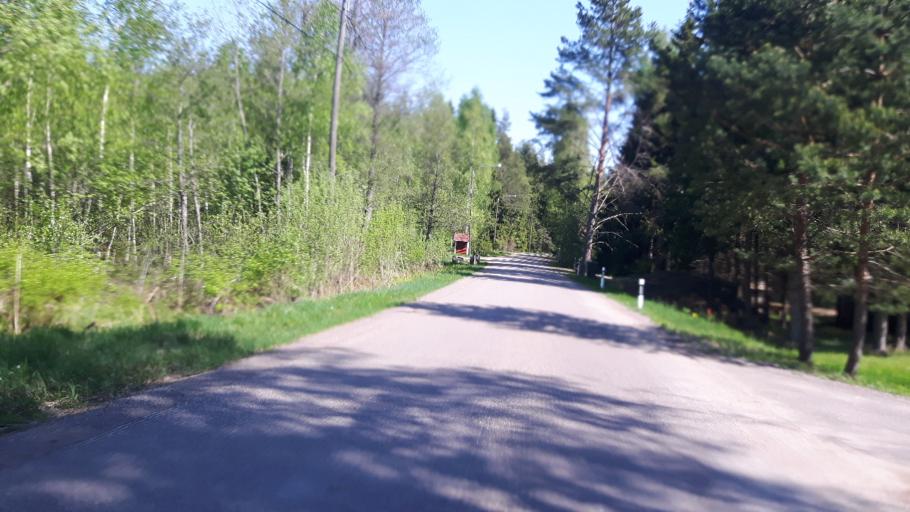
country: FI
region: Uusimaa
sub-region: Loviisa
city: Ruotsinpyhtaeae
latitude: 60.4959
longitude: 26.4303
